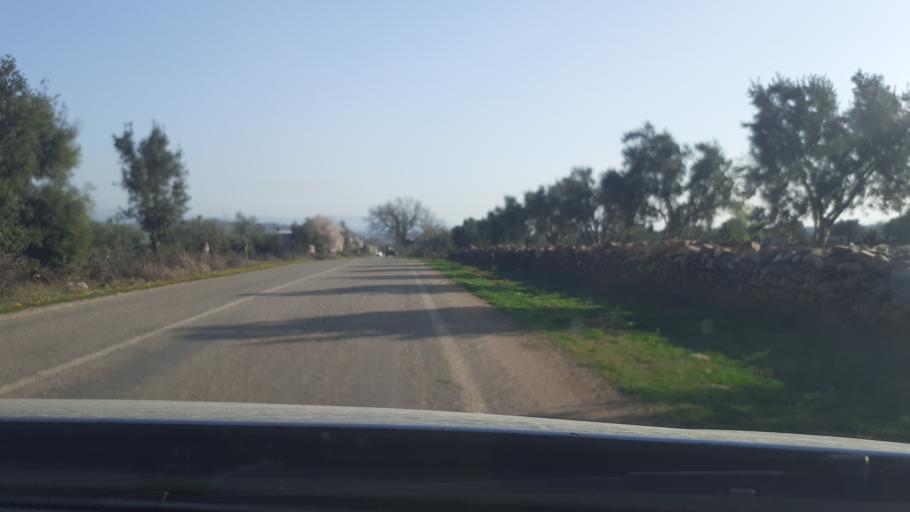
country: TR
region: Hatay
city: Aktepe
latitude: 36.7246
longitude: 36.4850
